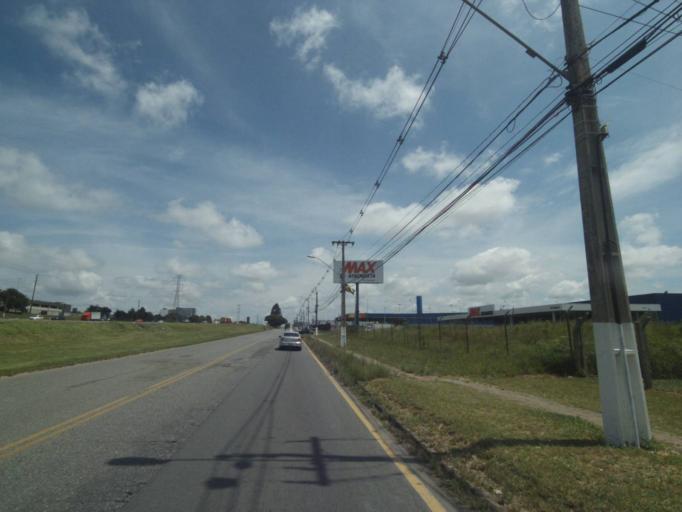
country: BR
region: Parana
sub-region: Curitiba
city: Curitiba
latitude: -25.4575
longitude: -49.3596
